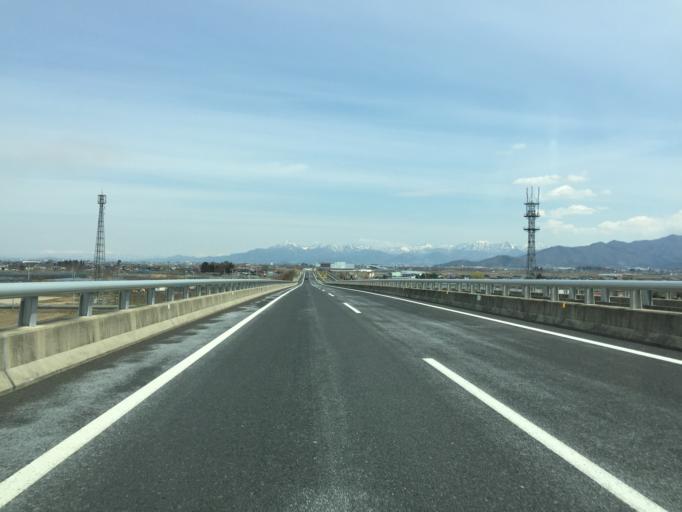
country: JP
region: Yamagata
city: Tendo
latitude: 38.3115
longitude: 140.3182
